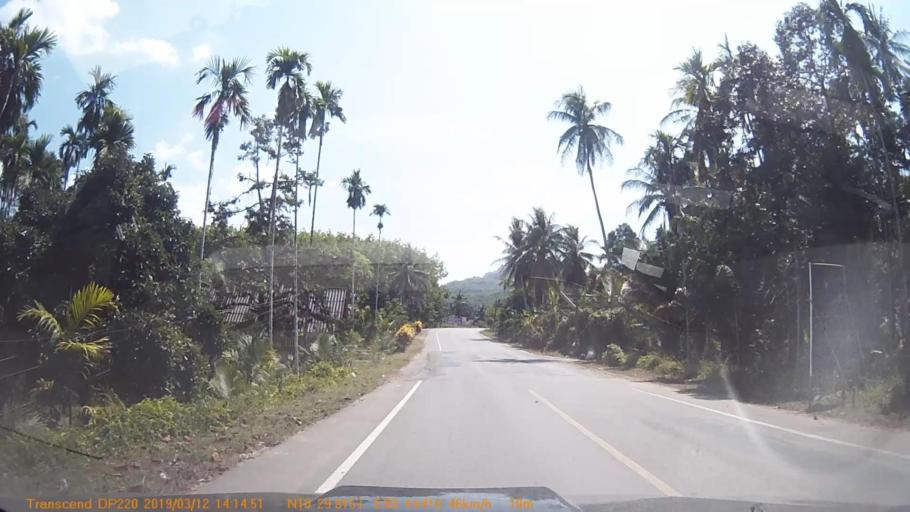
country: TH
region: Chumphon
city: Chumphon
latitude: 10.4967
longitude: 99.0772
